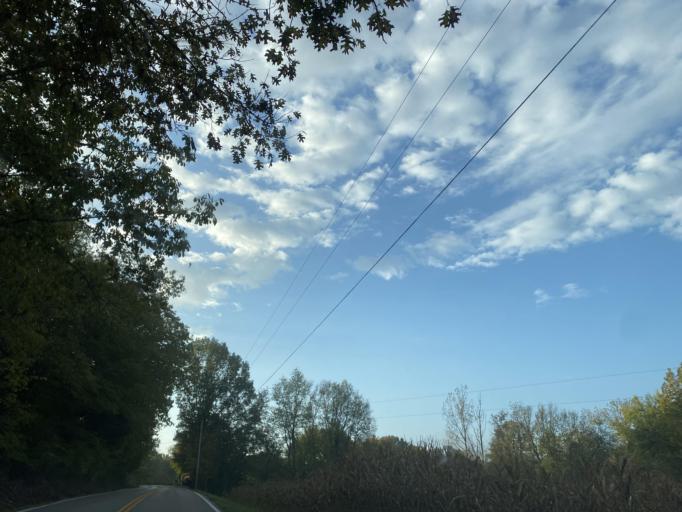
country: US
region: Kentucky
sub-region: Pendleton County
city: Falmouth
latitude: 38.7839
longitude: -84.3342
